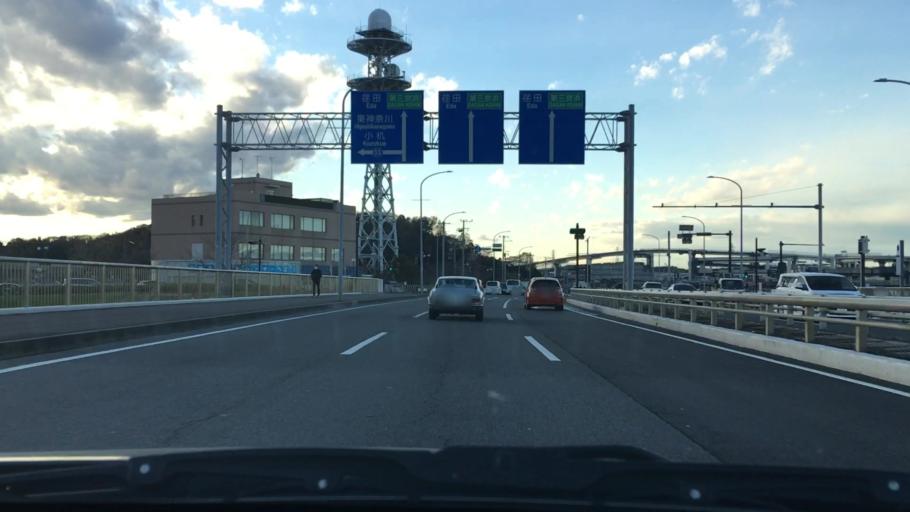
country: JP
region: Kanagawa
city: Yokohama
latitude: 35.5122
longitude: 139.6012
